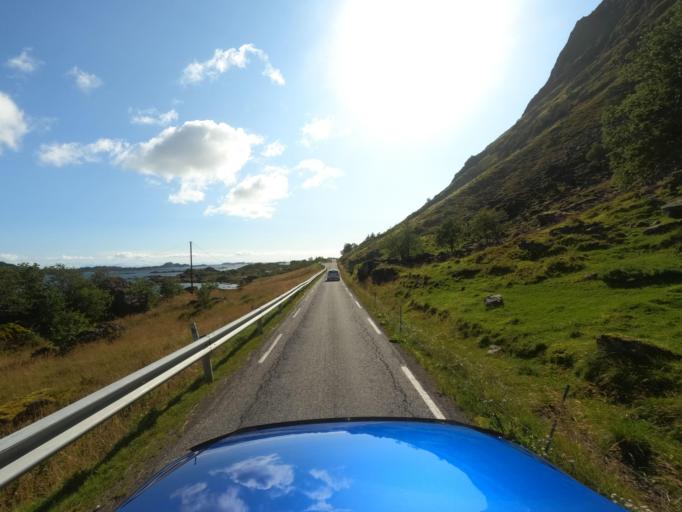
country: NO
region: Nordland
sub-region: Vestvagoy
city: Leknes
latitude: 68.1314
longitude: 13.7408
